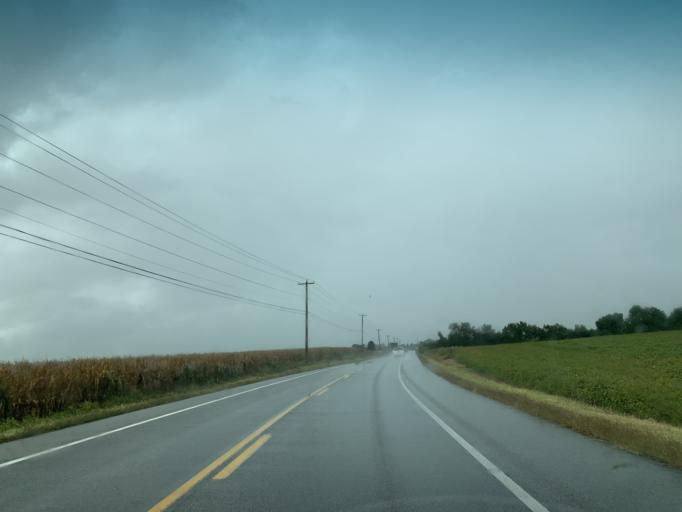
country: US
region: Maryland
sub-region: Queen Anne's County
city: Kingstown
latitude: 39.2061
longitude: -75.8639
